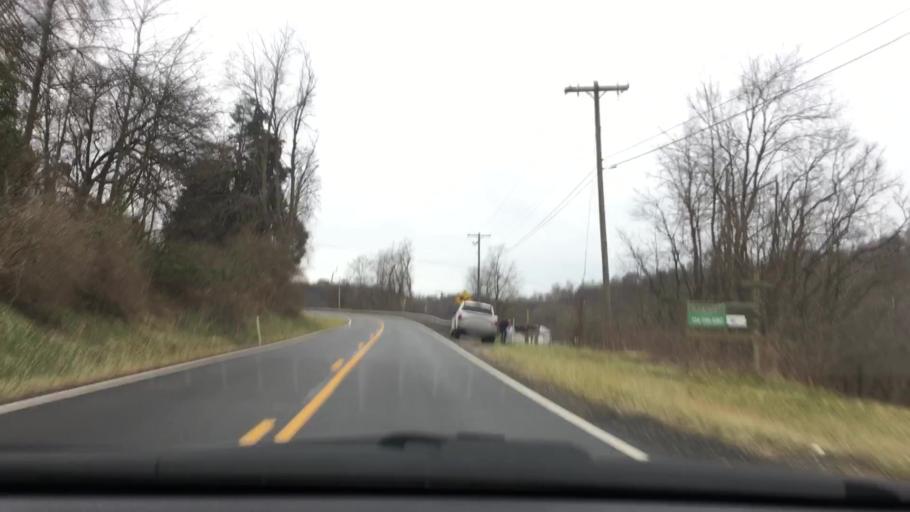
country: US
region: Pennsylvania
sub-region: Greene County
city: Morrisville
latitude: 39.8758
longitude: -80.1606
